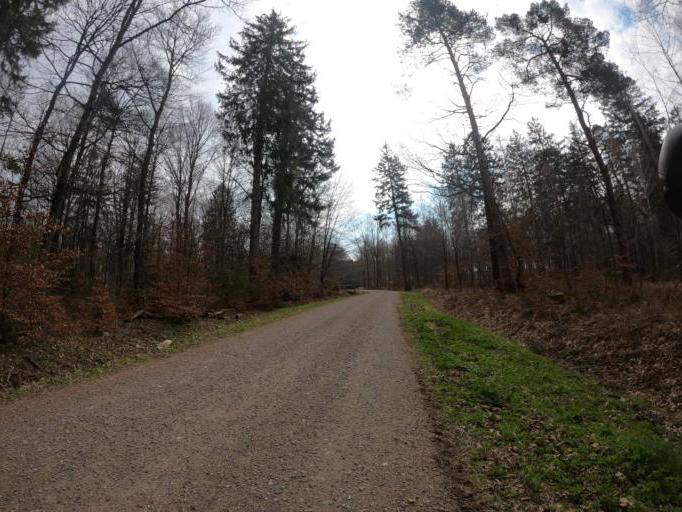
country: DE
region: North Rhine-Westphalia
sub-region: Regierungsbezirk Koln
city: Roetgen
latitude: 50.6553
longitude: 6.2160
